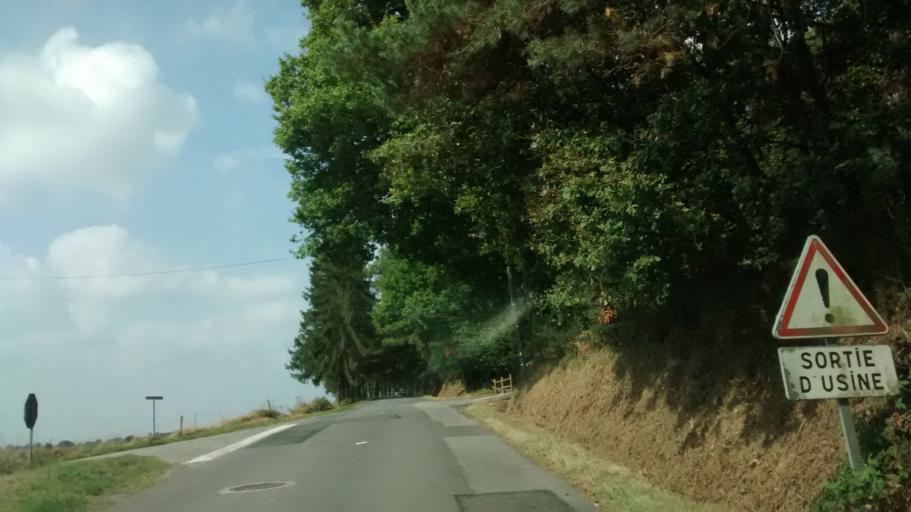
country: FR
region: Brittany
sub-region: Departement d'Ille-et-Vilaine
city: Chatillon-en-Vendelais
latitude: 48.2266
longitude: -1.1904
